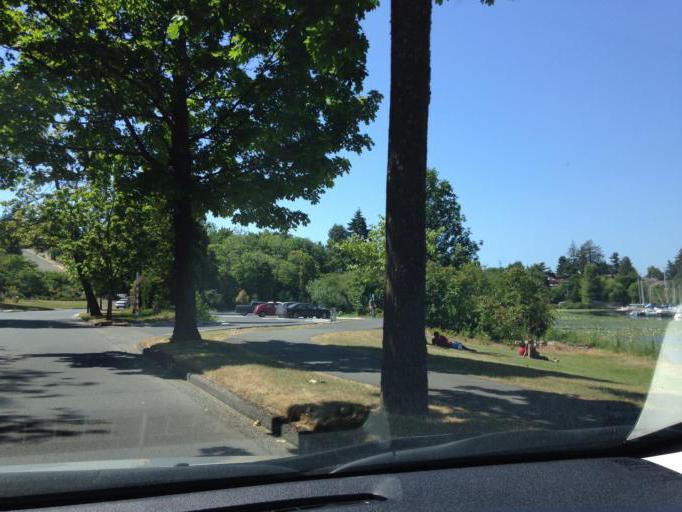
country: US
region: Washington
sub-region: King County
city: Mercer Island
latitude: 47.5614
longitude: -122.2660
